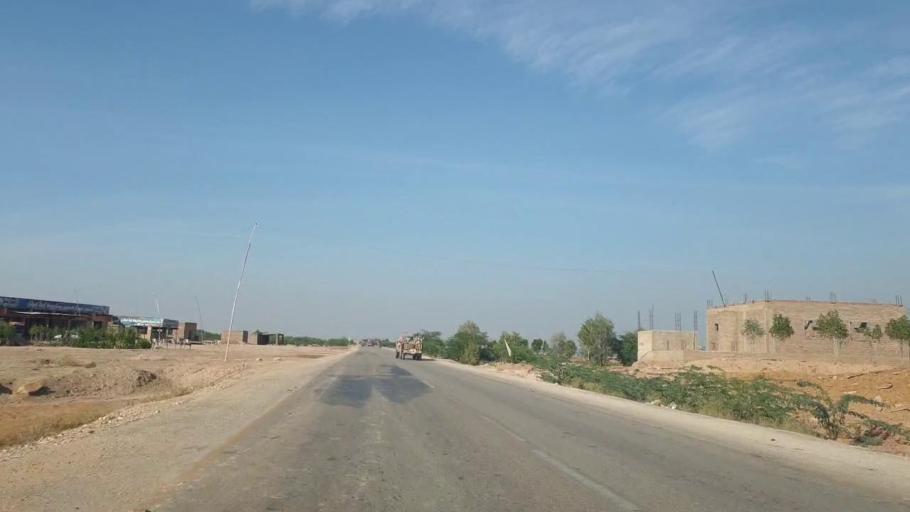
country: PK
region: Sindh
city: Sehwan
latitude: 26.3762
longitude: 67.8731
